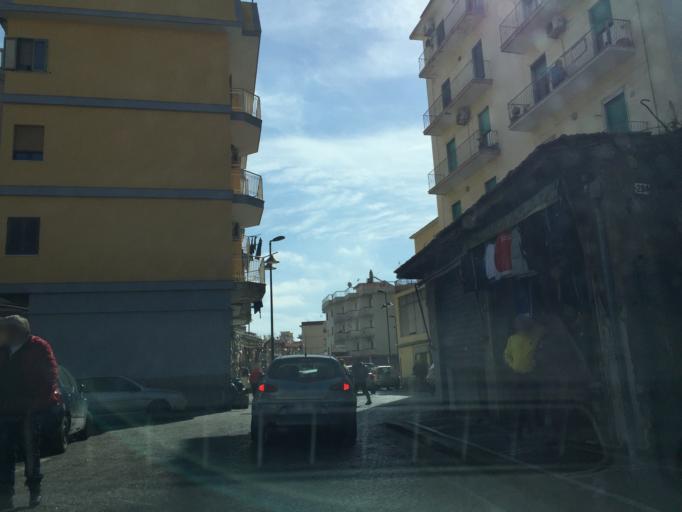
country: IT
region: Campania
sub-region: Provincia di Napoli
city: Ercolano
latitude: 40.8113
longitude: 14.3519
